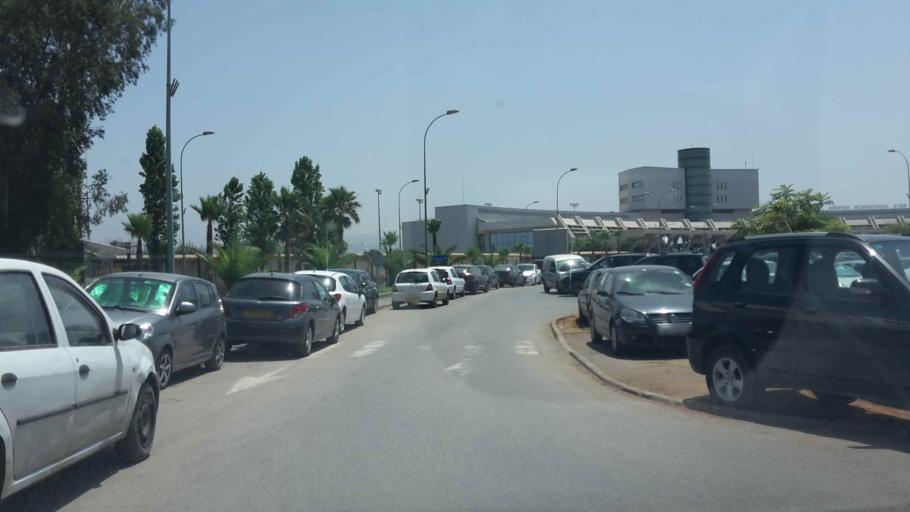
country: DZ
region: Alger
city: Dar el Beida
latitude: 36.7005
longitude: 3.2085
